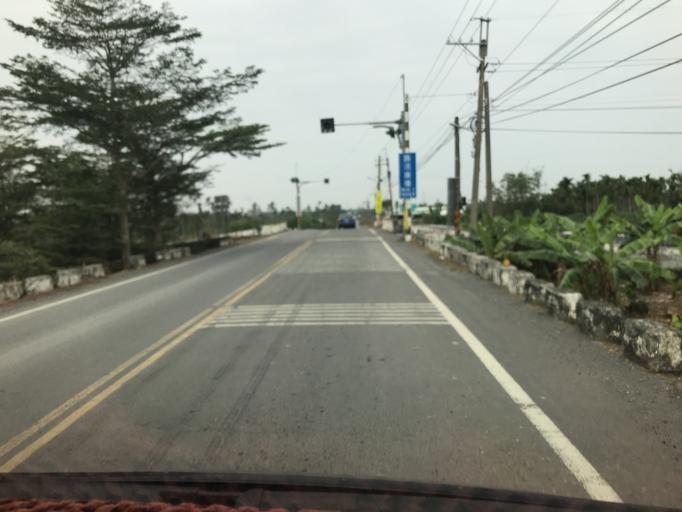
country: TW
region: Taiwan
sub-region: Pingtung
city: Pingtung
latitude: 22.4678
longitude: 120.6095
